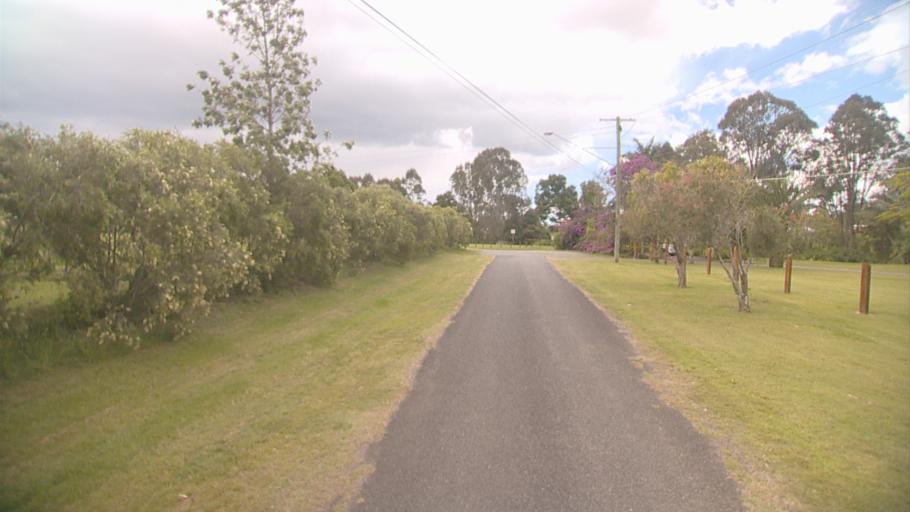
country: AU
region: Queensland
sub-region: Logan
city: Waterford West
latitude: -27.6996
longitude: 153.1430
